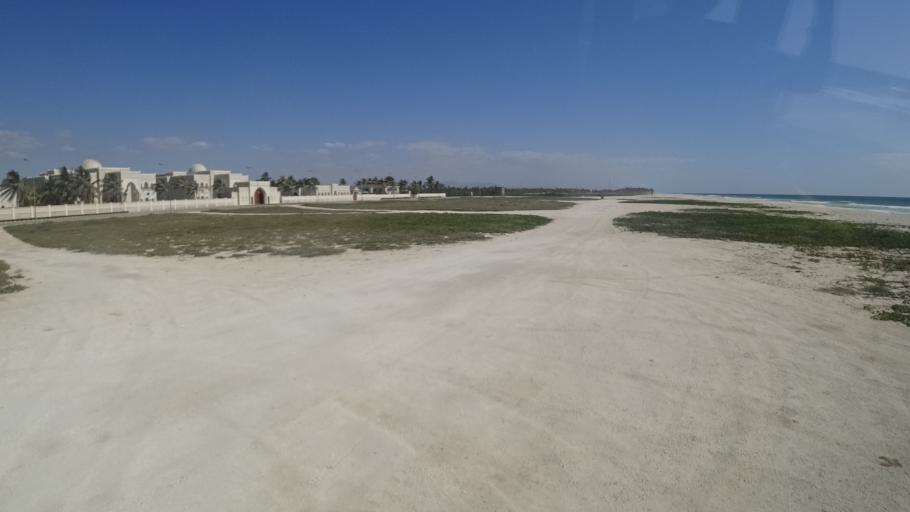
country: OM
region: Zufar
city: Salalah
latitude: 16.9938
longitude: 54.0624
